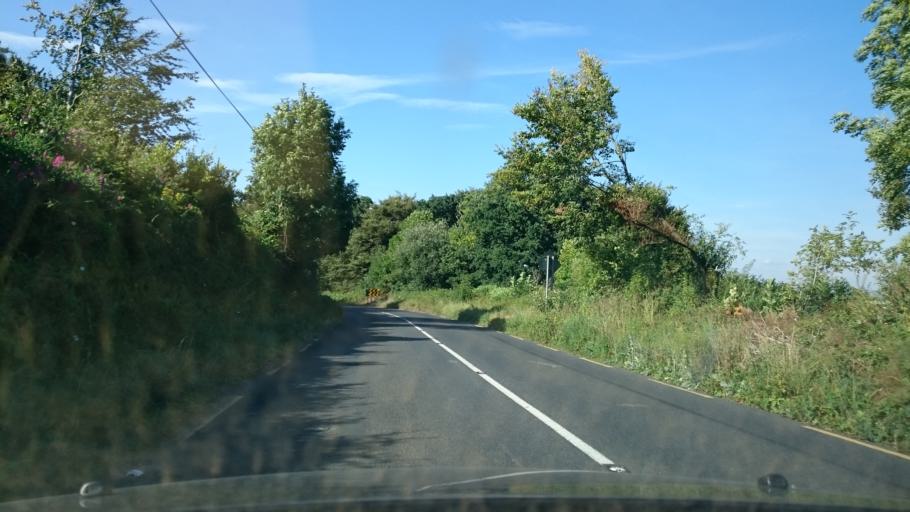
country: IE
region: Leinster
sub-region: Kilkenny
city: Graiguenamanagh
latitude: 52.5286
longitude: -6.9534
